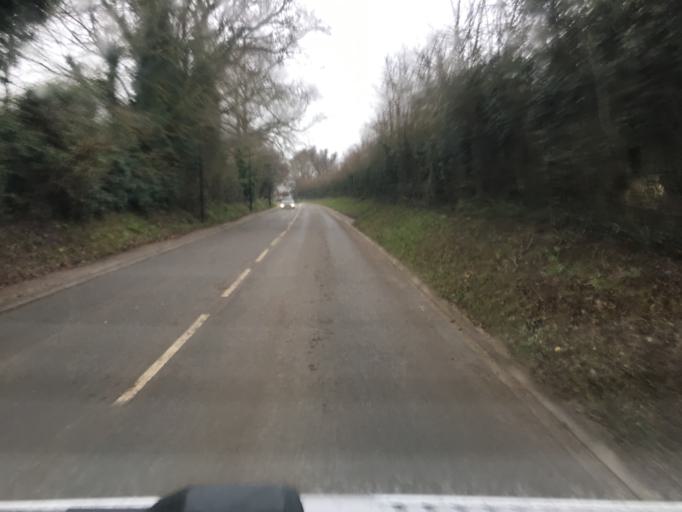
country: FR
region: Picardie
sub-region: Departement de la Somme
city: Saint-Valery-sur-Somme
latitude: 50.1764
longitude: 1.6411
